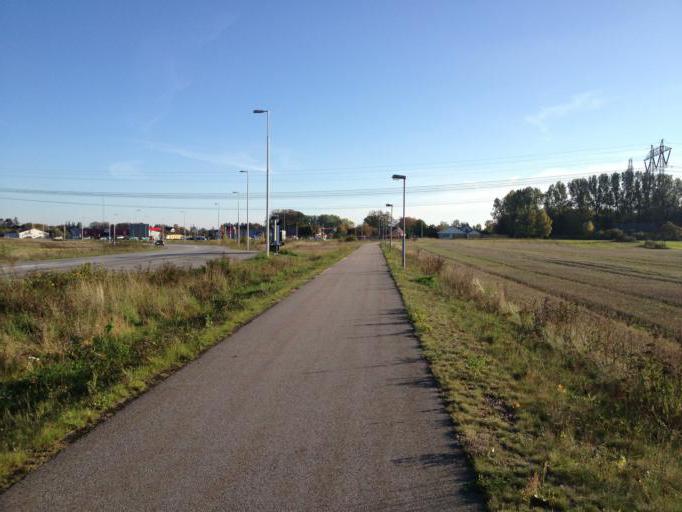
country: SE
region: Skane
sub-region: Kavlinge Kommun
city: Loddekopinge
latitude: 55.7427
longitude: 13.0298
